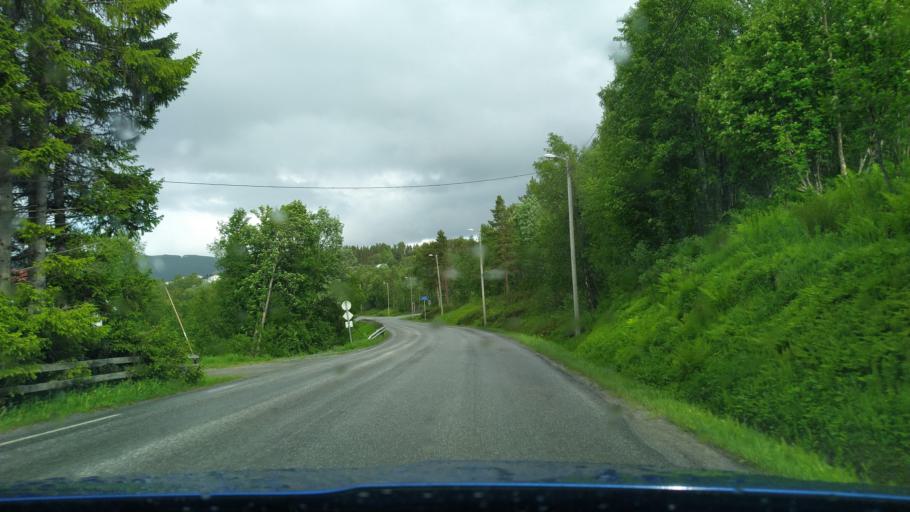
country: NO
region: Troms
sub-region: Sorreisa
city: Sorreisa
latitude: 69.1396
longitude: 18.1104
